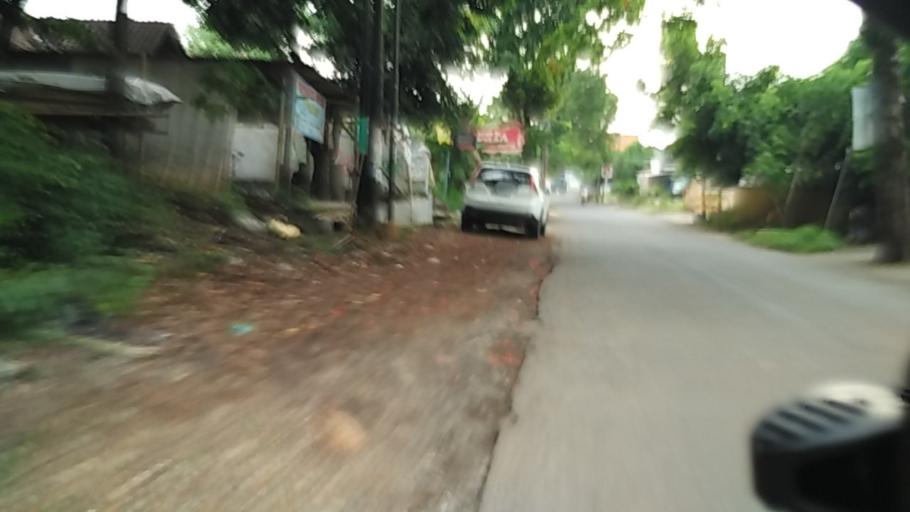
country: ID
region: Central Java
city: Semarang
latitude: -7.0633
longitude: 110.4369
